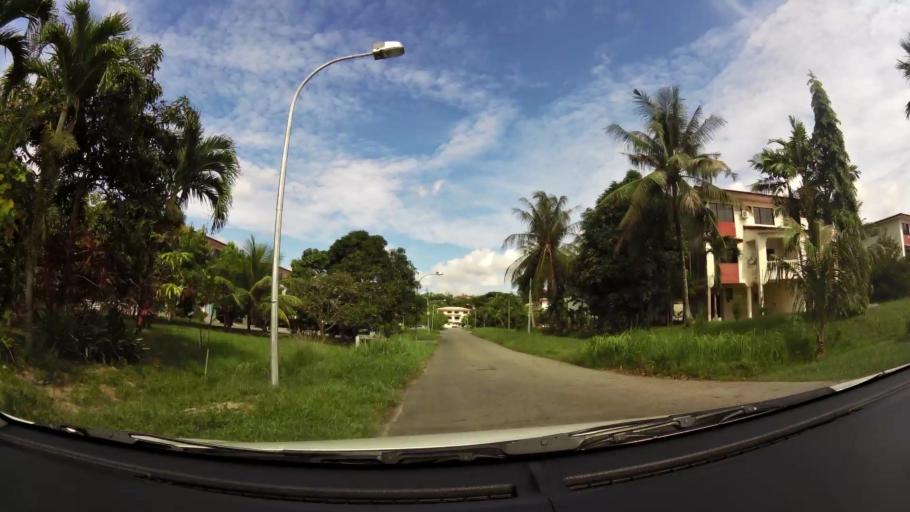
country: BN
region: Brunei and Muara
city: Bandar Seri Begawan
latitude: 4.9324
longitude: 114.9099
